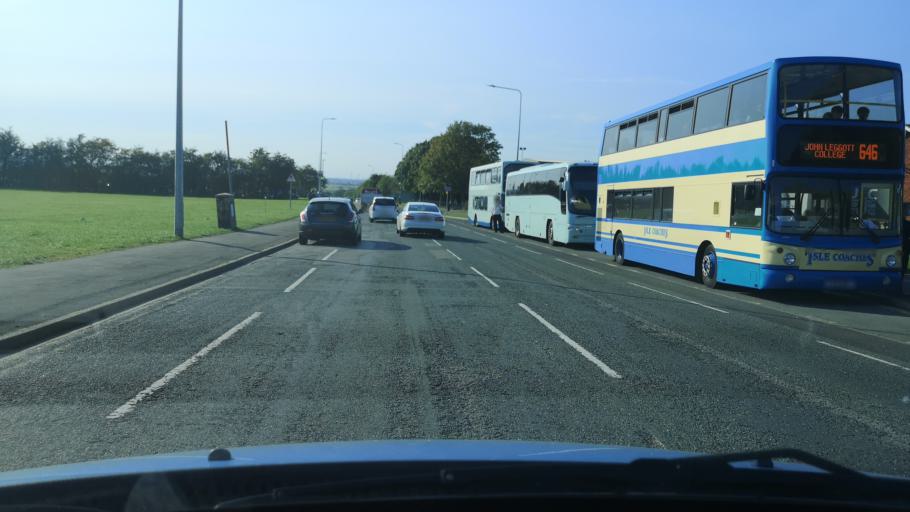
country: GB
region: England
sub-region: North Lincolnshire
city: Scunthorpe
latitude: 53.5739
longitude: -0.6669
